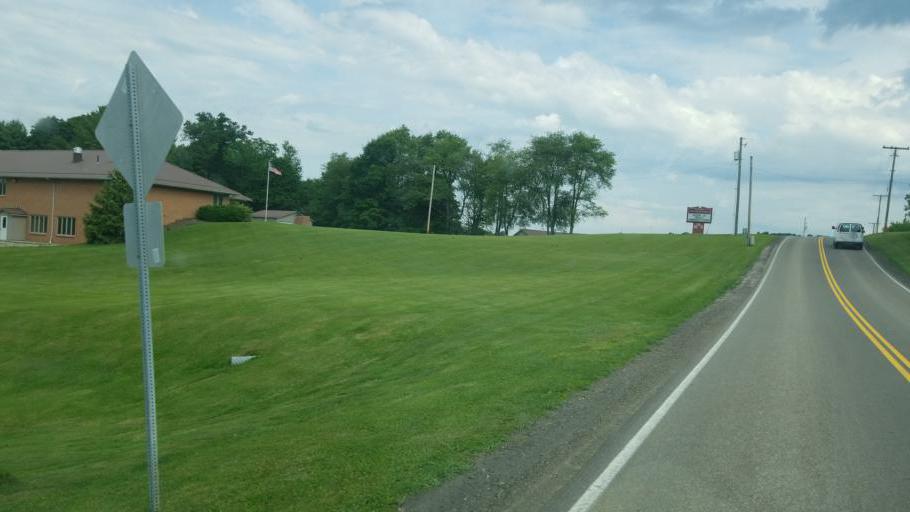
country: US
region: Ohio
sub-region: Knox County
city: Danville
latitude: 40.4576
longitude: -82.2629
